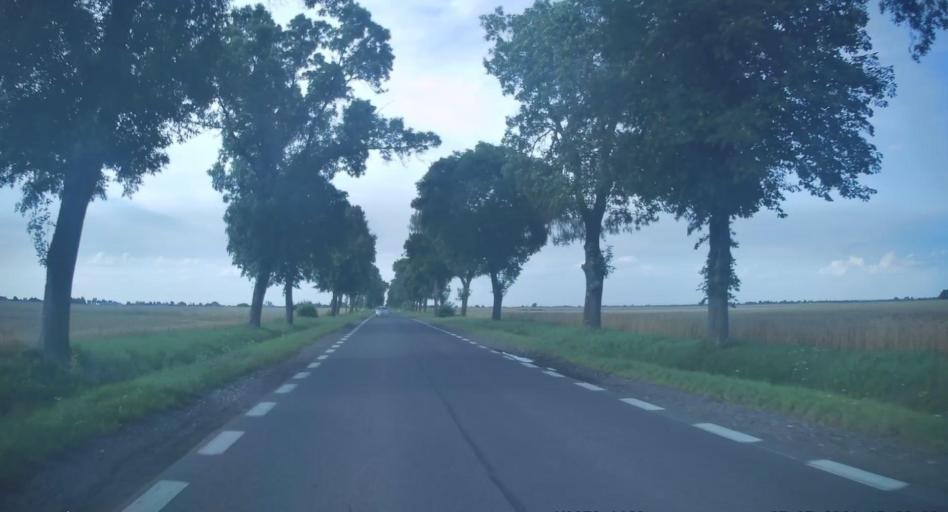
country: PL
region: Lodz Voivodeship
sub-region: Powiat tomaszowski
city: Rzeczyca
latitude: 51.6177
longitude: 20.2930
